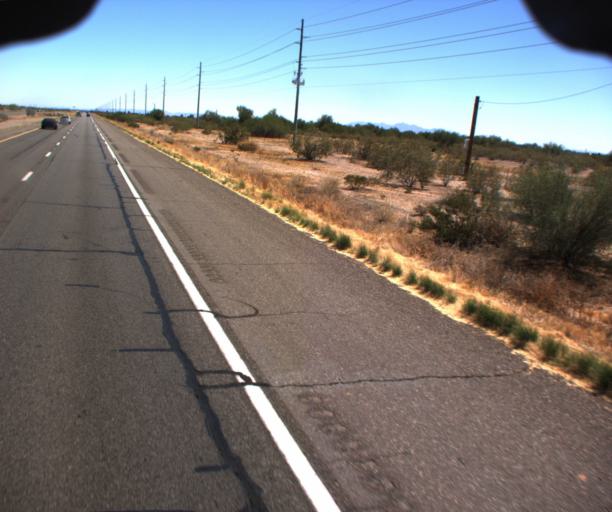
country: US
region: Arizona
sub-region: Maricopa County
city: Sun City West
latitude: 33.7246
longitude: -112.4606
